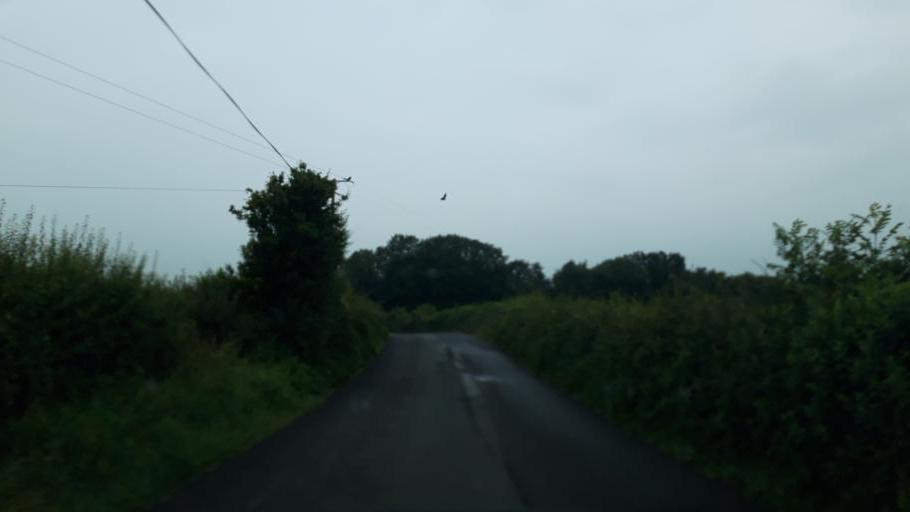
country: IE
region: Leinster
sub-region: Kilkenny
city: Thomastown
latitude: 52.6075
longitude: -7.1233
